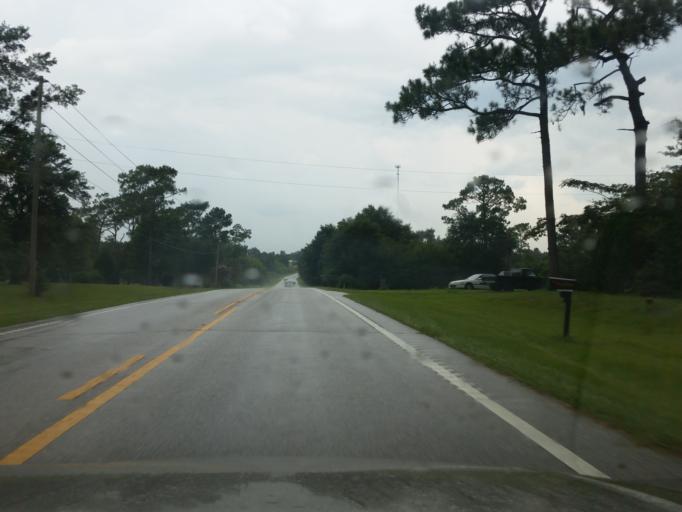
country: US
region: Alabama
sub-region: Baldwin County
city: Elberta
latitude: 30.5435
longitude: -87.5722
